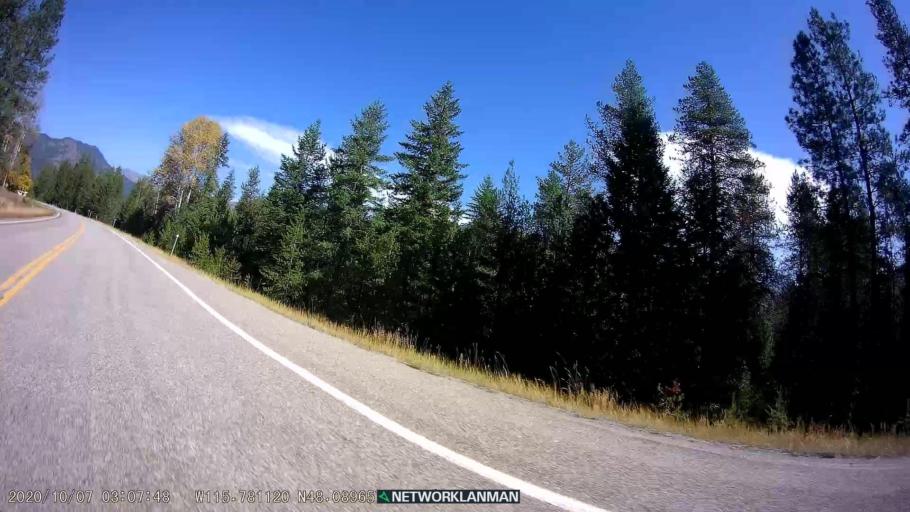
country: US
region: Montana
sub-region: Lincoln County
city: Libby
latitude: 48.0899
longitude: -115.7810
